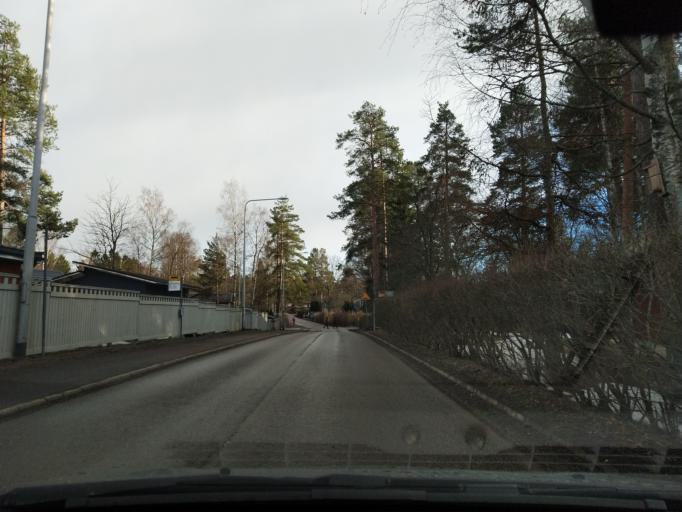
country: FI
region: Uusimaa
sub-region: Helsinki
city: Vantaa
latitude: 60.2833
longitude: 25.0673
